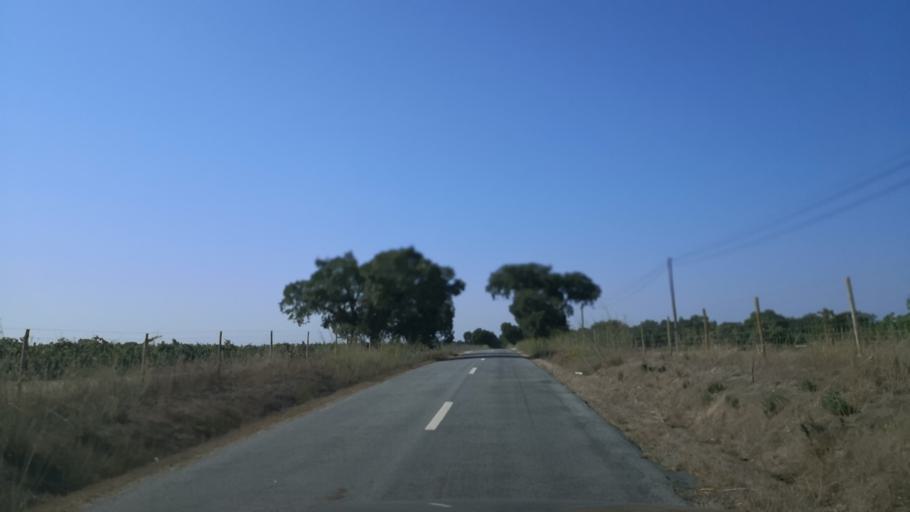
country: PT
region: Evora
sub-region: Vendas Novas
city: Vendas Novas
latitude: 38.7406
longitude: -8.6275
